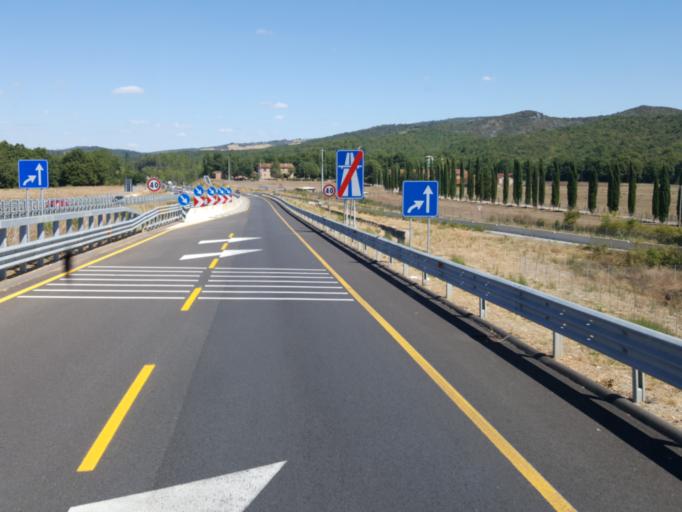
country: IT
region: Tuscany
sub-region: Provincia di Siena
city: Murlo
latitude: 43.1150
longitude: 11.2967
